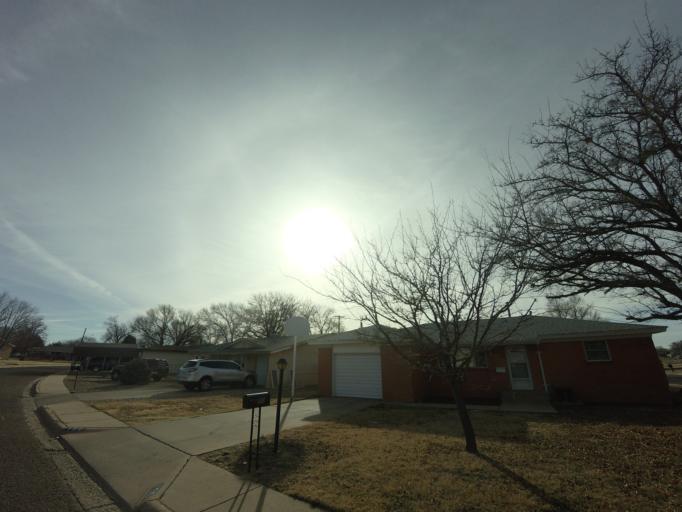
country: US
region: New Mexico
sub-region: Curry County
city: Clovis
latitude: 34.4144
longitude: -103.2179
